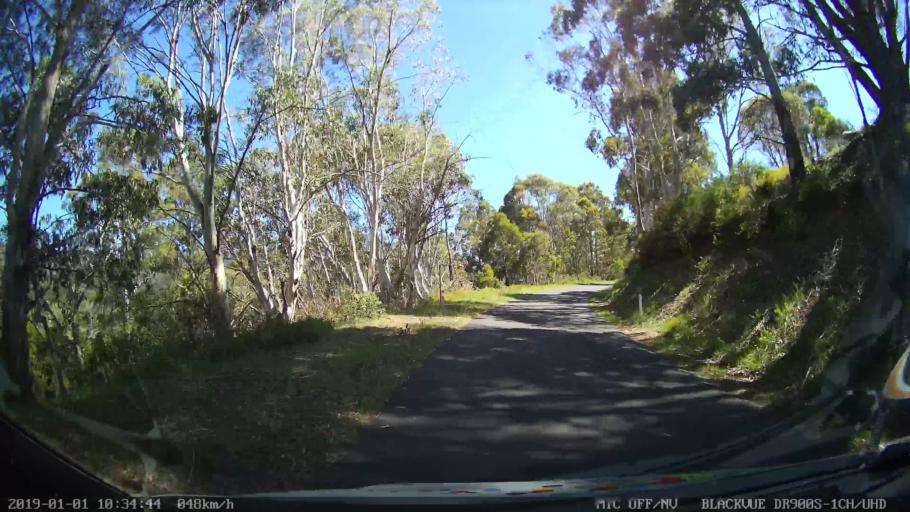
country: AU
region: New South Wales
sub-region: Snowy River
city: Jindabyne
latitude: -36.0484
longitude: 148.2844
